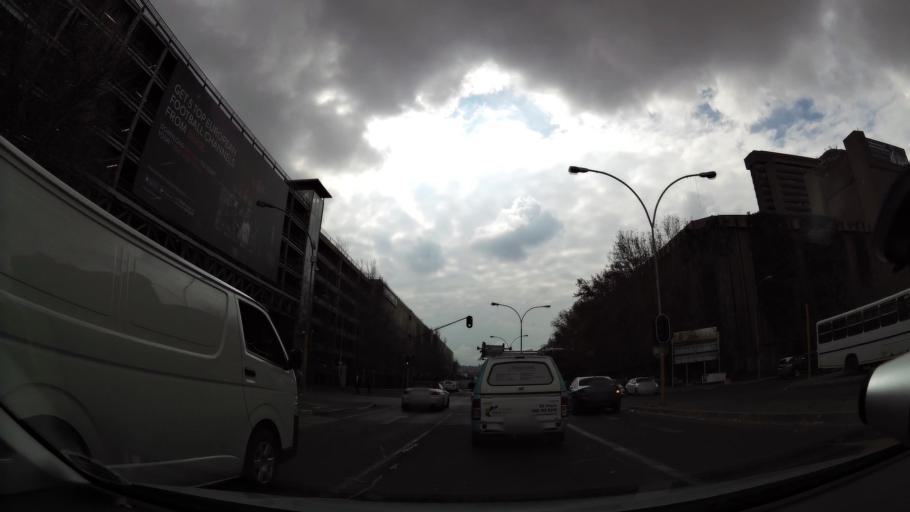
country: ZA
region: Orange Free State
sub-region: Mangaung Metropolitan Municipality
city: Bloemfontein
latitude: -29.1166
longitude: 26.2112
